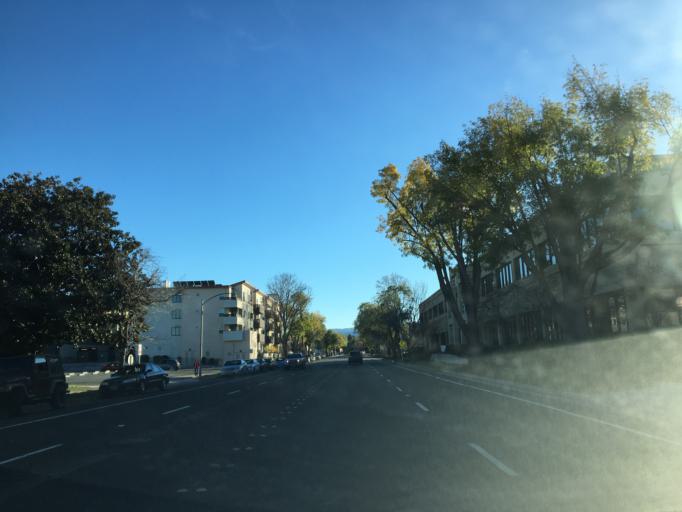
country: US
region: California
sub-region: Santa Clara County
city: Los Altos
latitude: 37.4258
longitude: -122.1042
